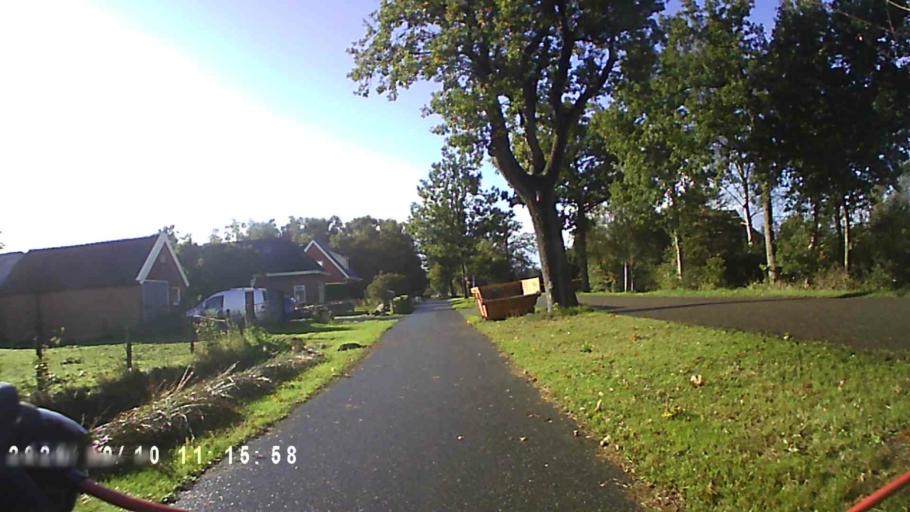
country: NL
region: Friesland
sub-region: Gemeente Smallingerland
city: Drachtstercompagnie
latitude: 53.1010
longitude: 6.2005
